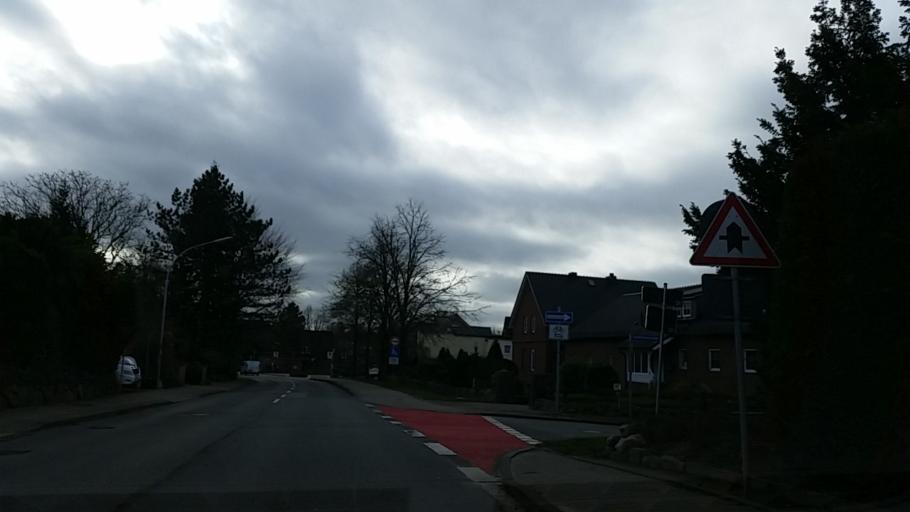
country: DE
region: Schleswig-Holstein
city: Bornsen
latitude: 53.4796
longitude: 10.2867
